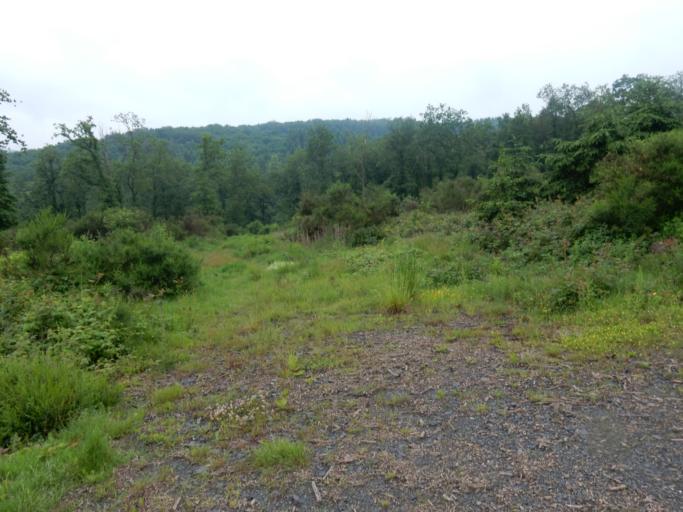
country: LU
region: Diekirch
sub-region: Canton de Wiltz
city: Wiltz
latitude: 49.9401
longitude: 5.9299
